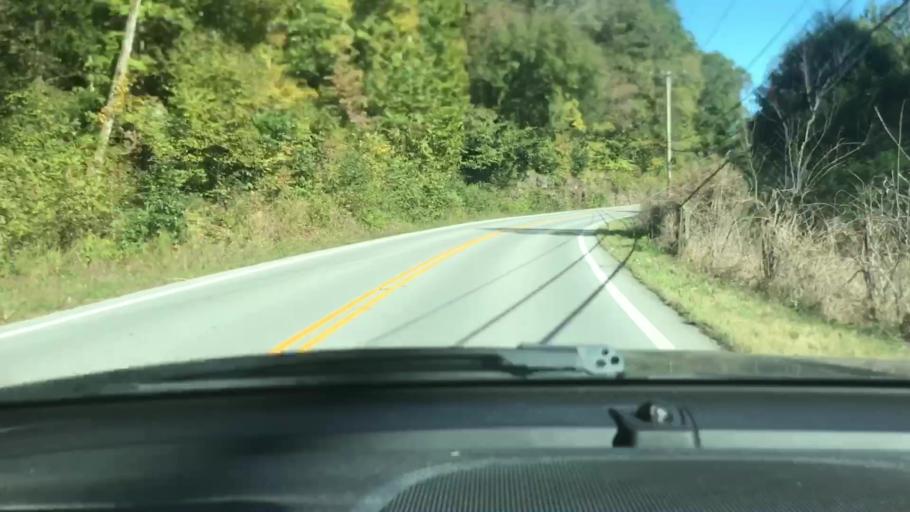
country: US
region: Tennessee
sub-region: Dickson County
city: Charlotte
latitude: 36.1818
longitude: -87.3161
